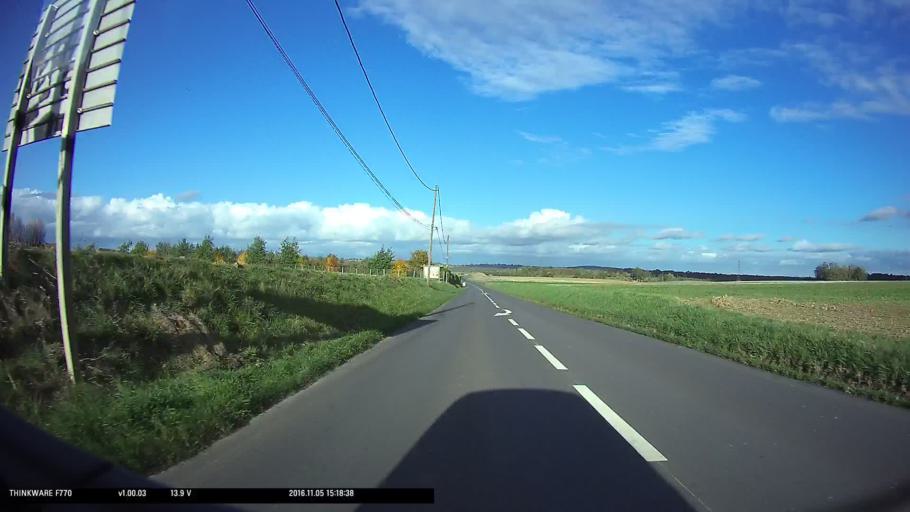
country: FR
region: Ile-de-France
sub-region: Departement du Val-d'Oise
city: Ableiges
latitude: 49.0743
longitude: 1.9692
